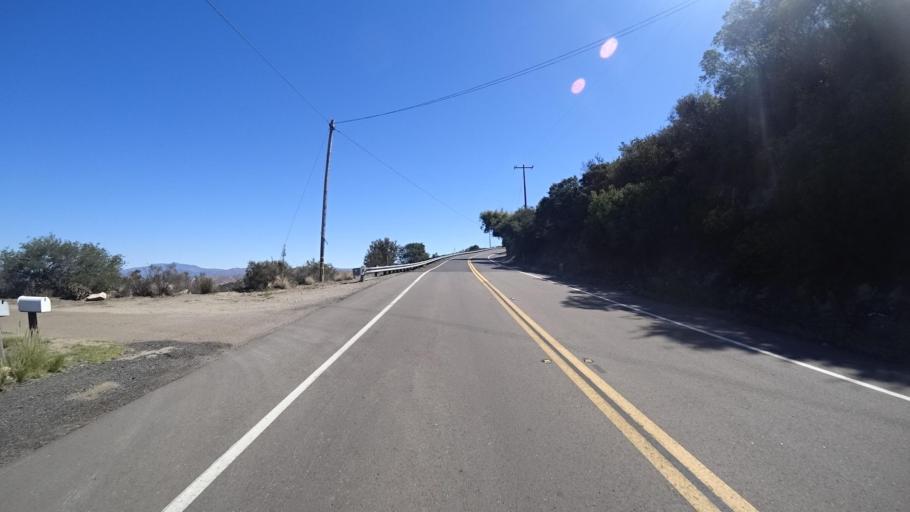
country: US
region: California
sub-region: San Diego County
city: Jamul
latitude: 32.7343
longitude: -116.8034
